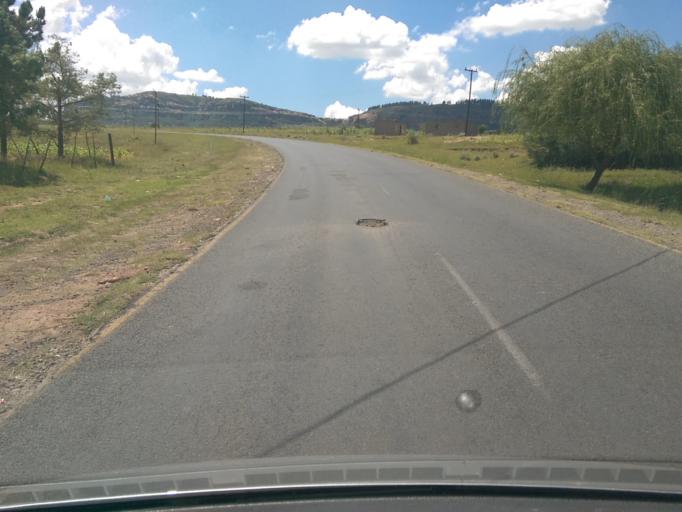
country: LS
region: Maseru
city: Nako
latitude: -29.4272
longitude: 27.6761
